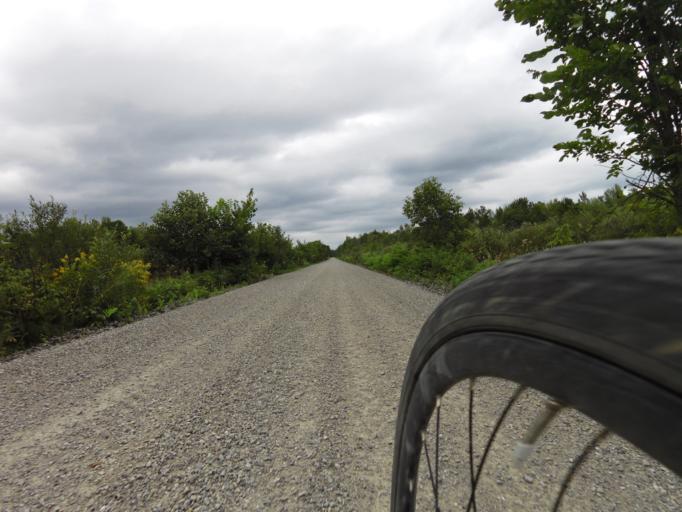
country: CA
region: Ontario
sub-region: Lanark County
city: Smiths Falls
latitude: 44.9551
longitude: -76.0469
